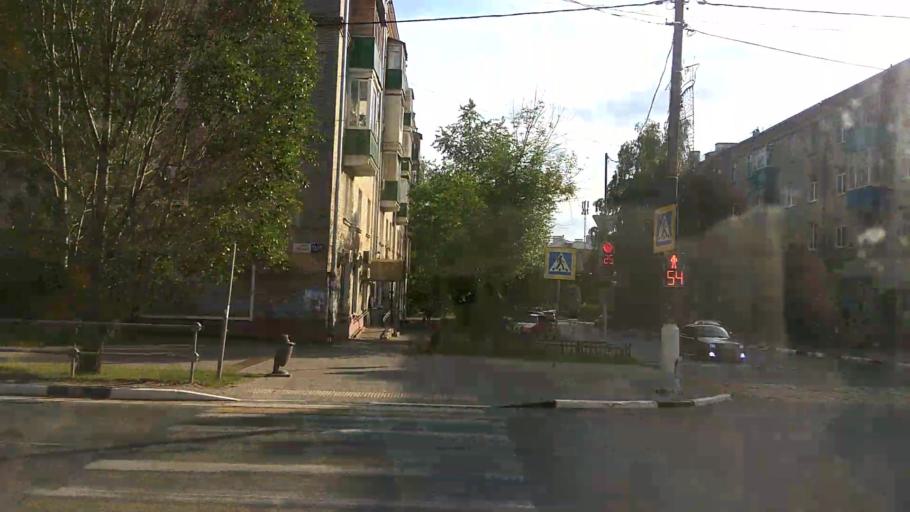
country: RU
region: Moskovskaya
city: Mytishchi
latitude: 55.9125
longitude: 37.7329
